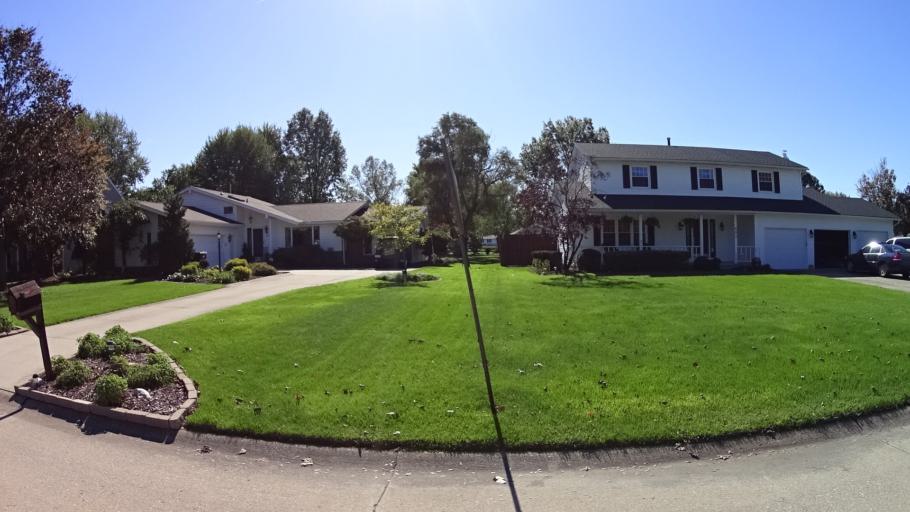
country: US
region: Ohio
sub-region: Lorain County
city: Amherst
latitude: 41.4111
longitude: -82.2221
